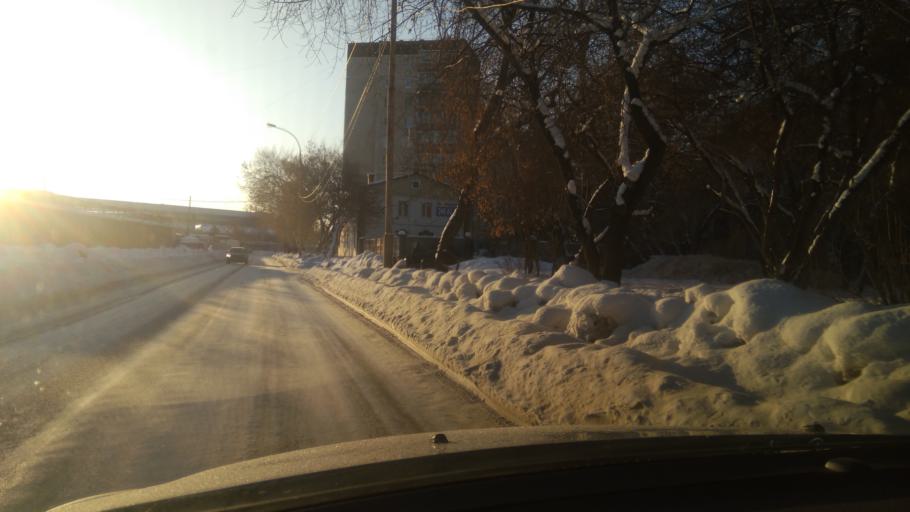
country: RU
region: Sverdlovsk
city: Yekaterinburg
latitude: 56.8821
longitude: 60.5680
